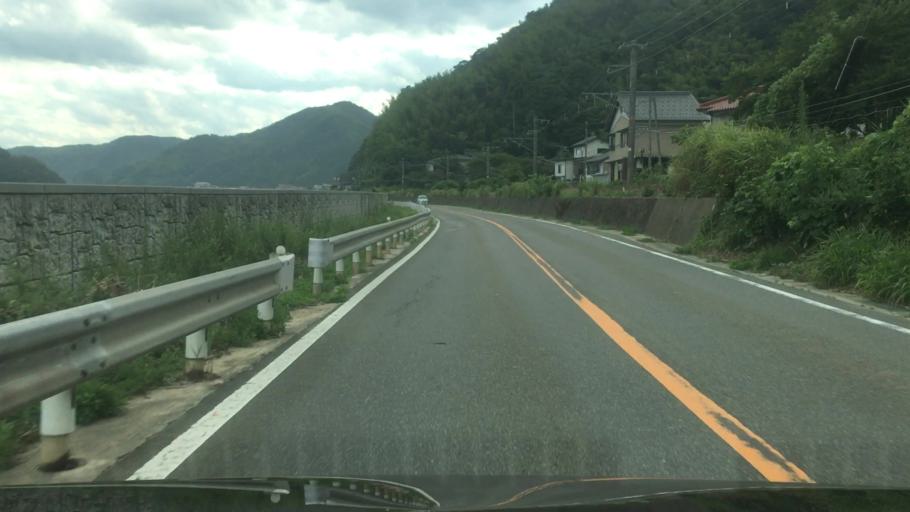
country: JP
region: Hyogo
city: Toyooka
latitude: 35.6160
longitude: 134.8096
